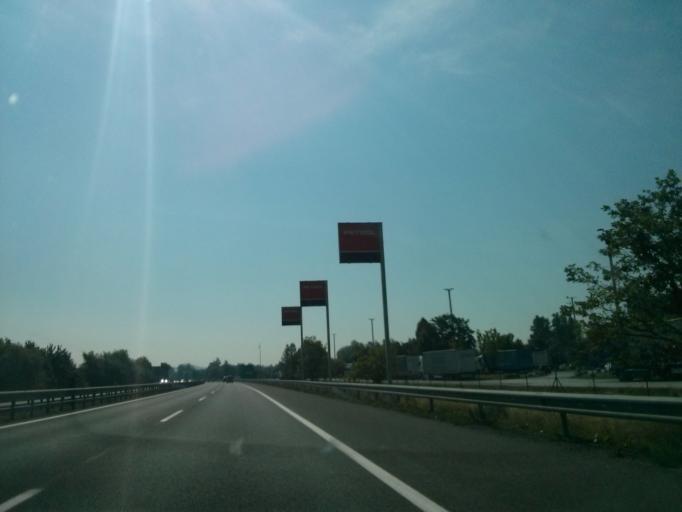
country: SI
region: Ljubljana
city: Ljubljana
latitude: 46.0295
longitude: 14.4782
